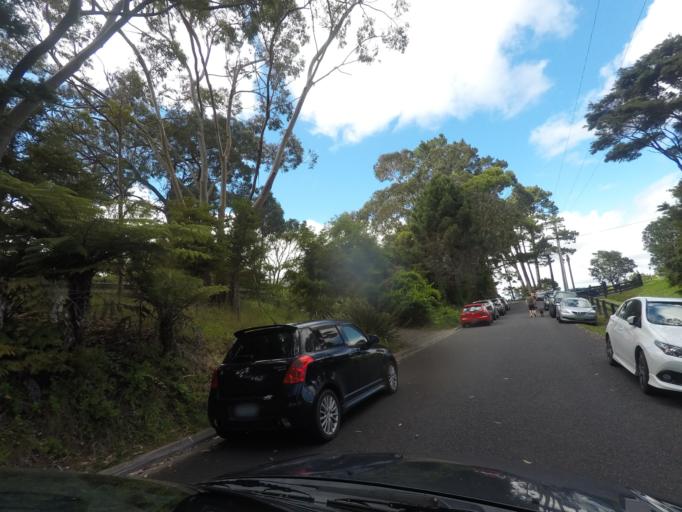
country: NZ
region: Auckland
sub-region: Auckland
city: Rothesay Bay
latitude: -36.7664
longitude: 174.6410
